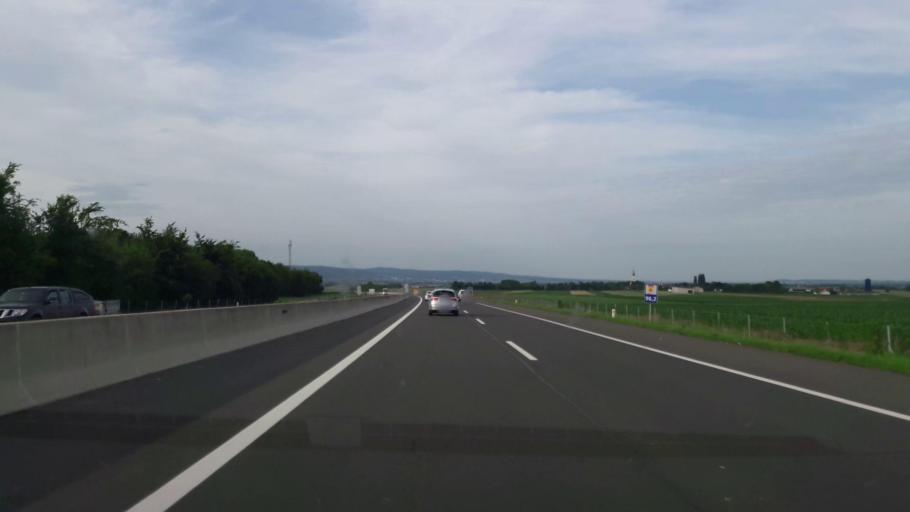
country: AT
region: Burgenland
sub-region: Politischer Bezirk Mattersburg
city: Pottelsdorf
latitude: 47.7656
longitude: 16.4229
